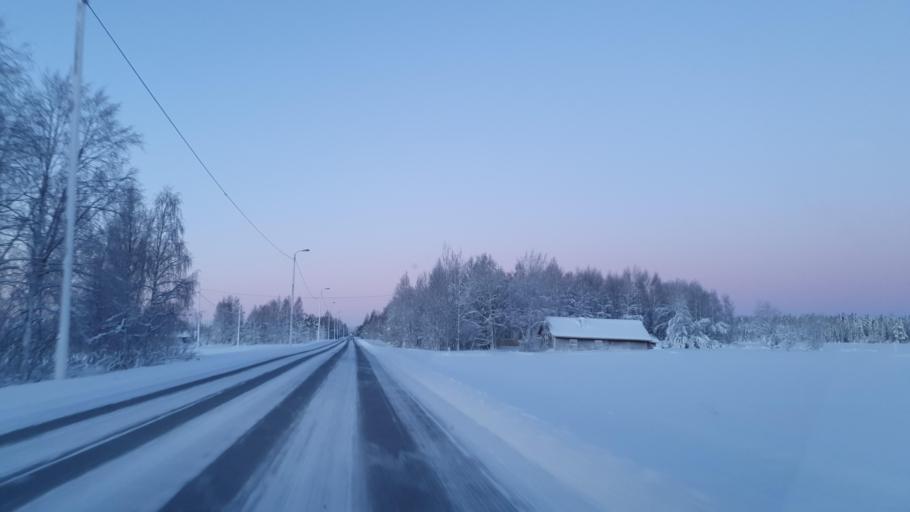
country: FI
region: Lapland
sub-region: Torniolaakso
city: Ylitornio
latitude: 66.1852
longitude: 23.8096
